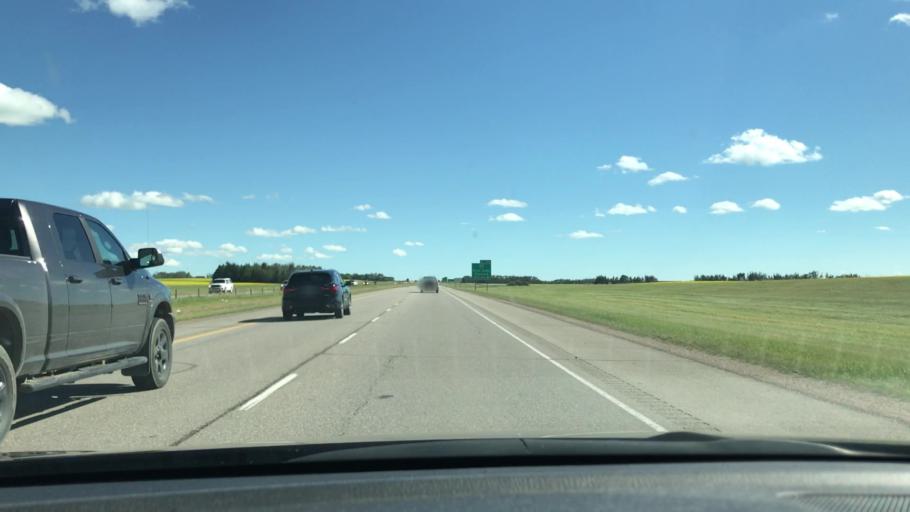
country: CA
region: Alberta
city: Penhold
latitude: 52.1654
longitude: -113.8147
